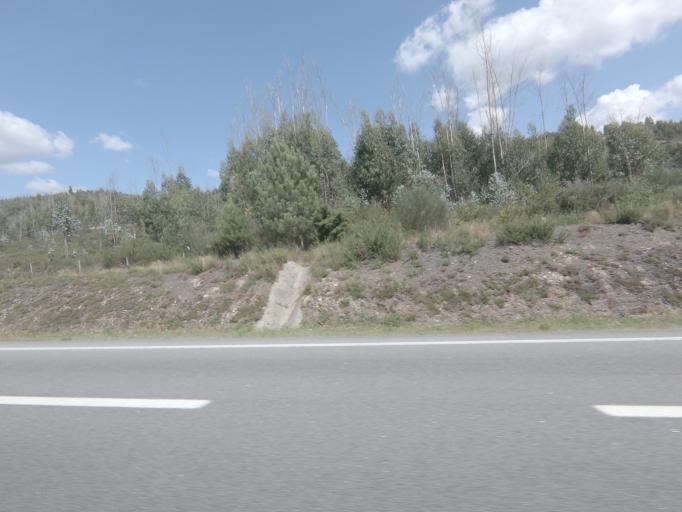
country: PT
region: Porto
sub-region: Valongo
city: Campo
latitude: 41.1904
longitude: -8.4805
